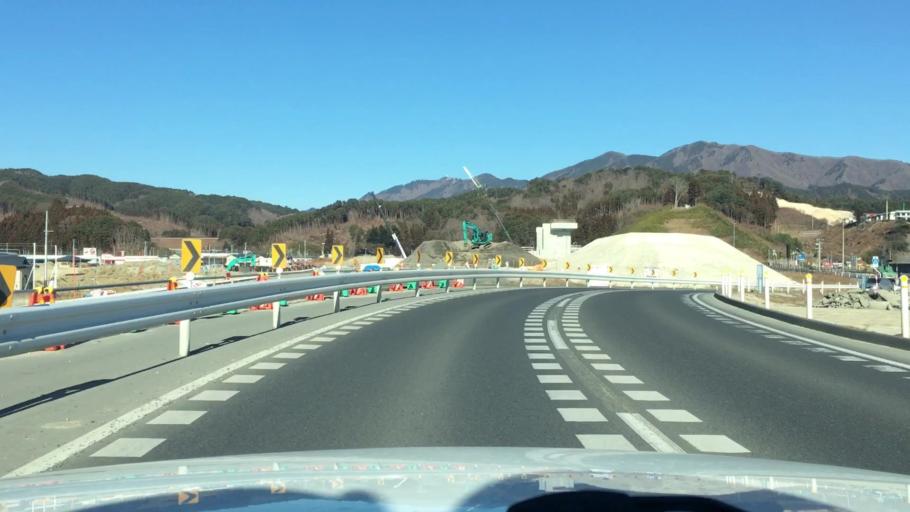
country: JP
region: Iwate
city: Yamada
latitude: 39.4718
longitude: 141.9533
